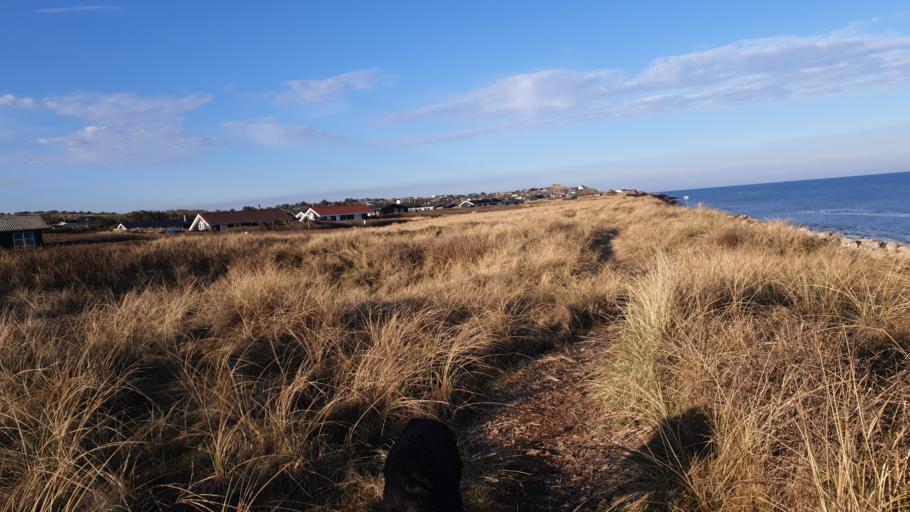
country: DK
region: North Denmark
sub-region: Hjorring Kommune
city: Hjorring
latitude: 57.4893
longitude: 9.8201
